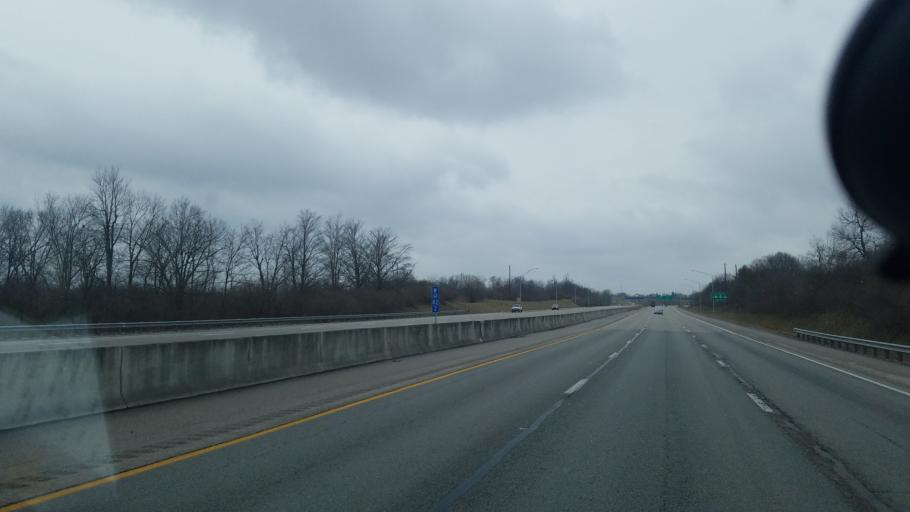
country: US
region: Kentucky
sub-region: Fayette County
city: Lexington-Fayette
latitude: 38.0584
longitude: -84.4147
